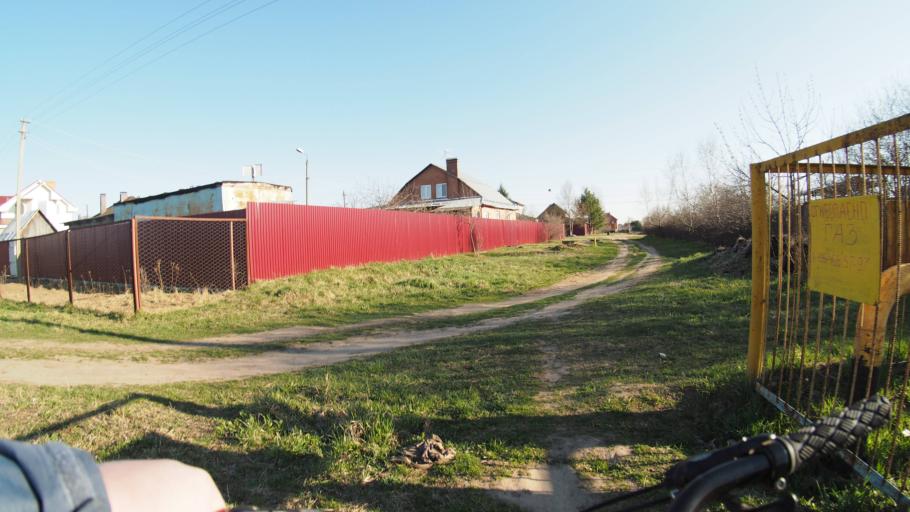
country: RU
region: Moskovskaya
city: Malyshevo
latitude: 55.5049
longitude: 38.3328
